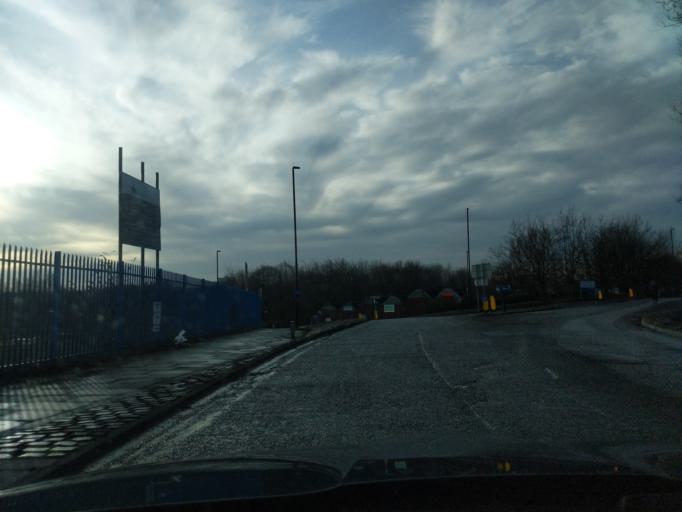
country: GB
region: England
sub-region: Borough of North Tyneside
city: Wallsend
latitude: 54.9851
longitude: -1.5375
